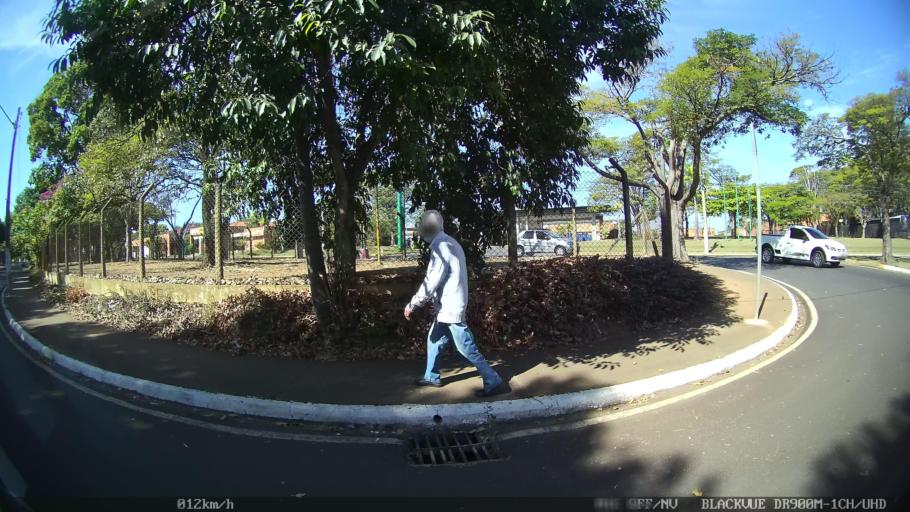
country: BR
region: Sao Paulo
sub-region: Franca
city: Franca
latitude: -20.5400
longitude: -47.4174
